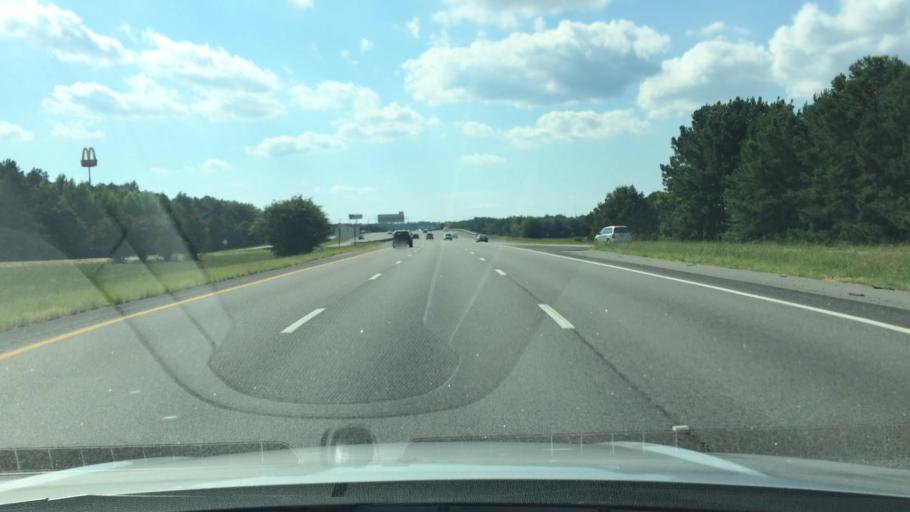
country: US
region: South Carolina
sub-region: Lexington County
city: Cayce
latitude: 33.9306
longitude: -81.0720
